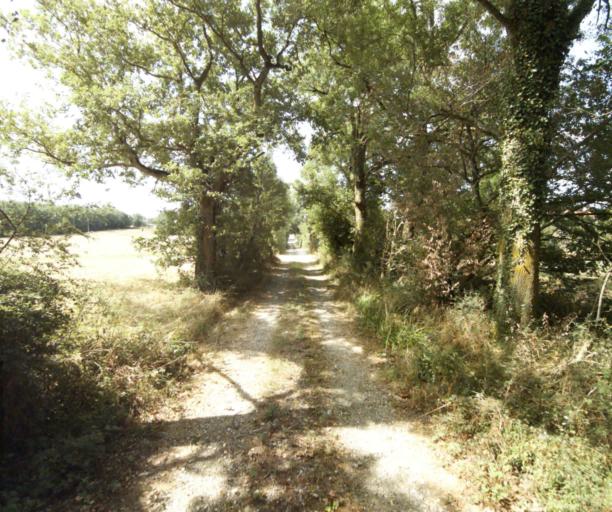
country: FR
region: Midi-Pyrenees
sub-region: Departement du Tarn
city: Dourgne
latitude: 43.4906
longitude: 2.1096
